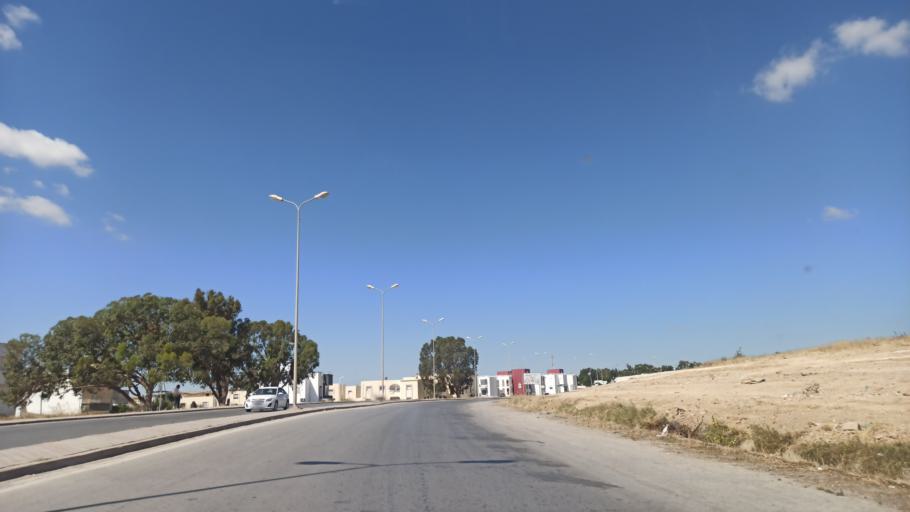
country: TN
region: Manouba
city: Manouba
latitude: 36.7839
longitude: 10.0775
